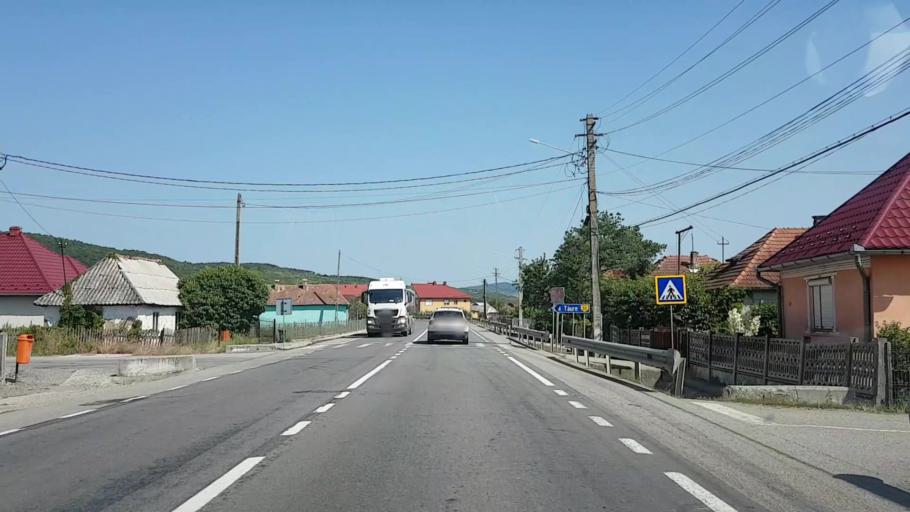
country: RO
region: Bistrita-Nasaud
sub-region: Comuna Sintereag
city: Sintereag
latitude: 47.1791
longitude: 24.2940
